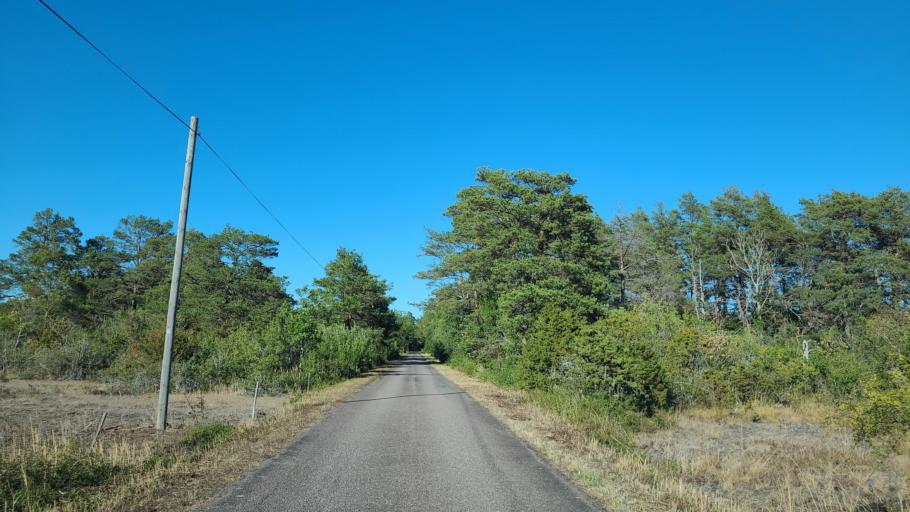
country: SE
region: Kalmar
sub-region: Borgholms Kommun
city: Borgholm
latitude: 57.3188
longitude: 17.0550
